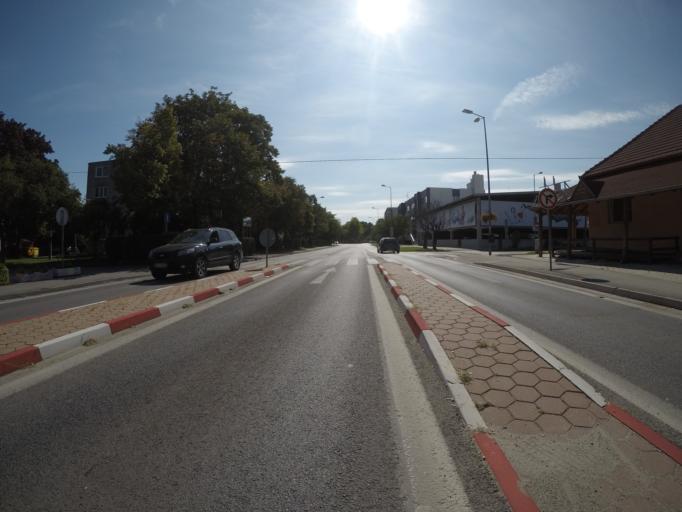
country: SK
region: Trnavsky
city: Dunajska Streda
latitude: 47.9976
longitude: 17.6135
